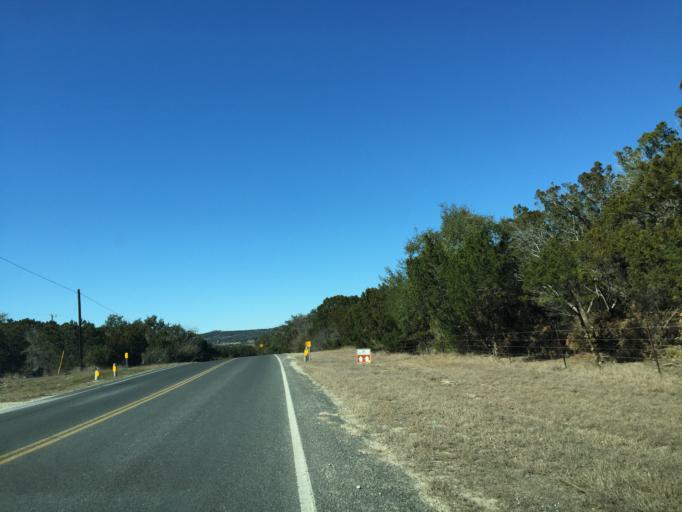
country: US
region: Texas
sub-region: Comal County
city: Bulverde
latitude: 29.7359
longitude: -98.4027
